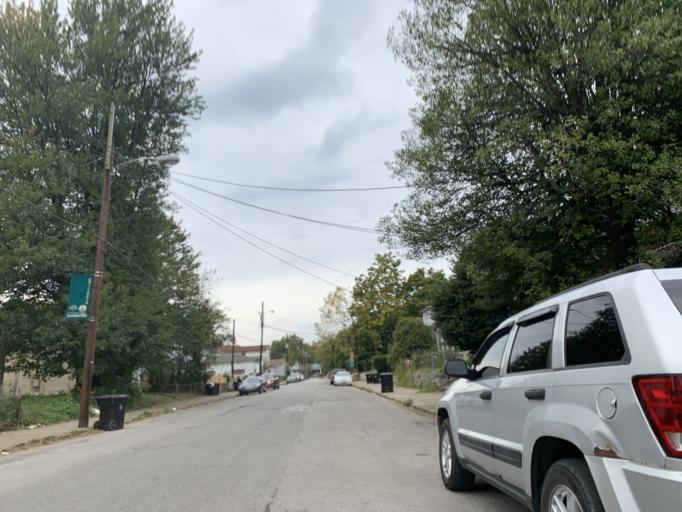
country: US
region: Kentucky
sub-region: Jefferson County
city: Louisville
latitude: 38.2419
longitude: -85.7823
